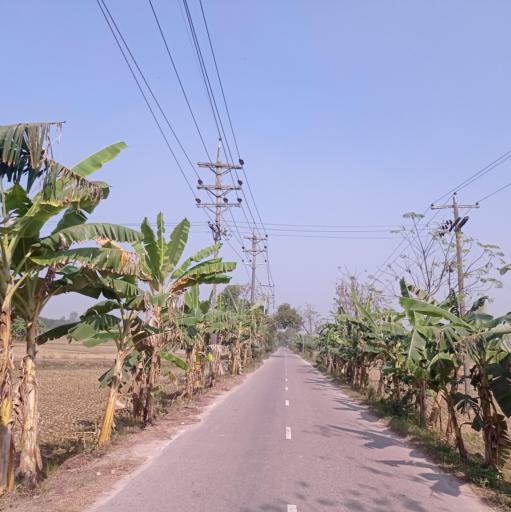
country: BD
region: Dhaka
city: Narsingdi
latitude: 24.0321
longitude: 90.6740
